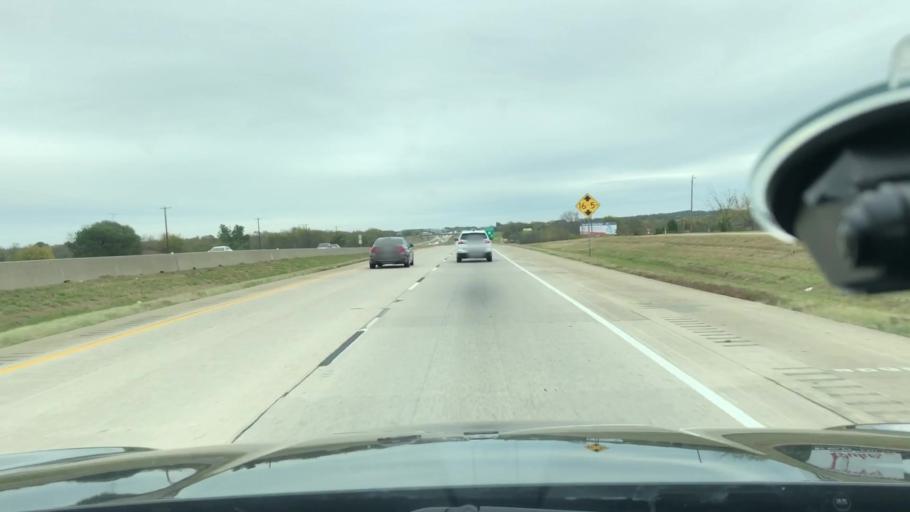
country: US
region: Texas
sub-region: Hopkins County
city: Sulphur Springs
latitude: 33.1208
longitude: -95.6830
